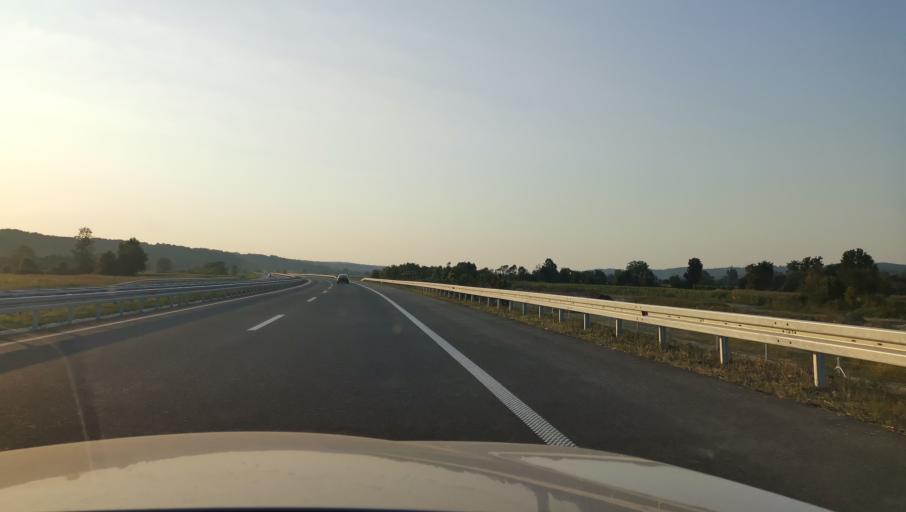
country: RS
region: Central Serbia
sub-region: Kolubarski Okrug
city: Ljig
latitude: 44.3068
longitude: 20.2276
